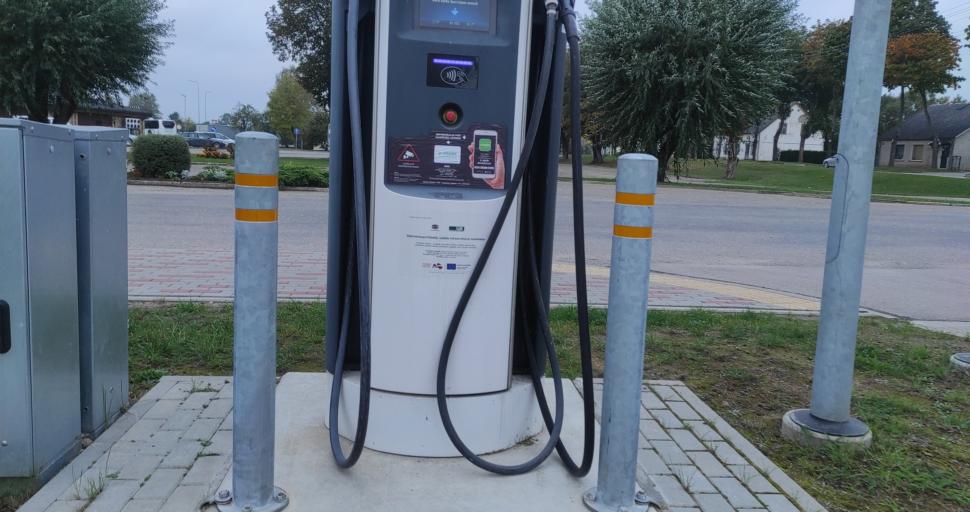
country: LV
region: Skrunda
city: Skrunda
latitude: 56.6748
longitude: 22.0142
